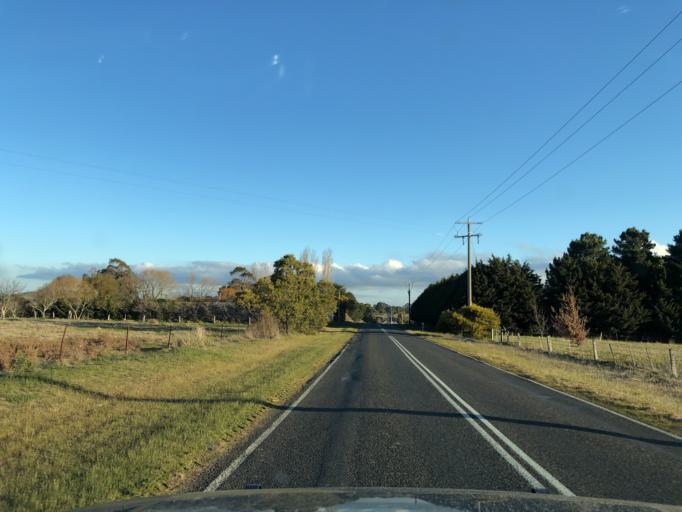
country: AU
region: Victoria
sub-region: Moorabool
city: Bacchus Marsh
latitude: -37.5835
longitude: 144.2372
